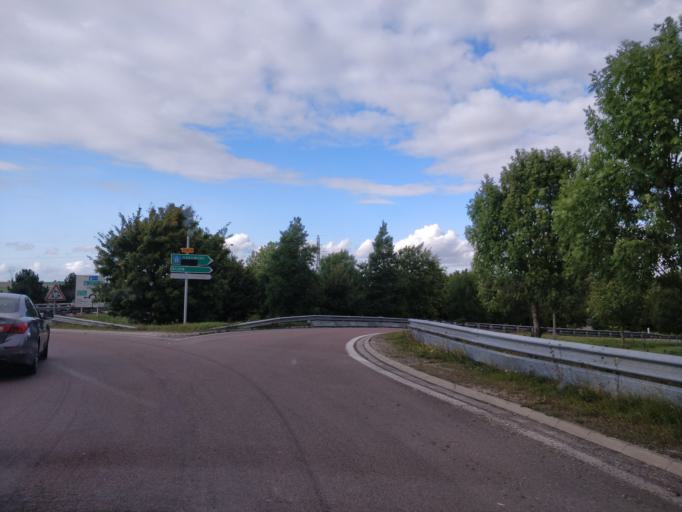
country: FR
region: Champagne-Ardenne
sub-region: Departement de l'Aube
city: Pont-Sainte-Marie
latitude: 48.3342
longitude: 4.1011
